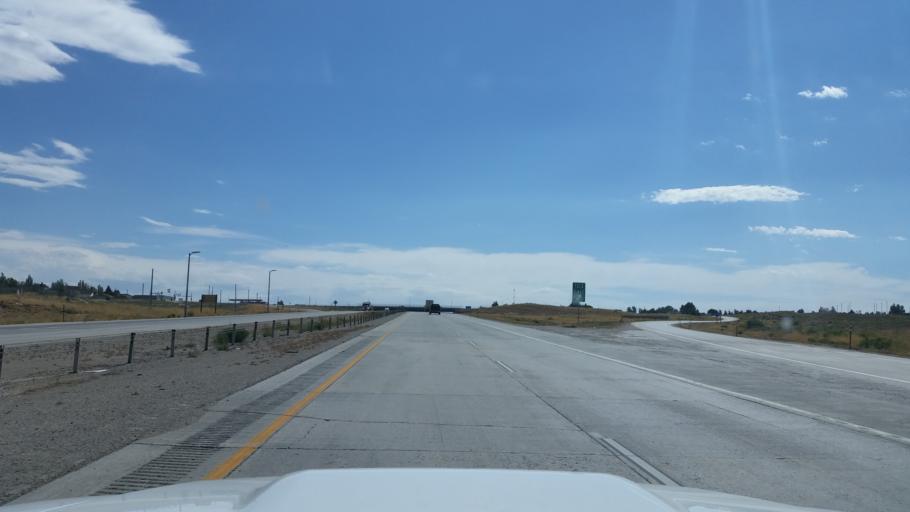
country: US
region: Wyoming
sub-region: Sweetwater County
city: Rock Springs
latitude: 41.6026
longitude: -109.2388
